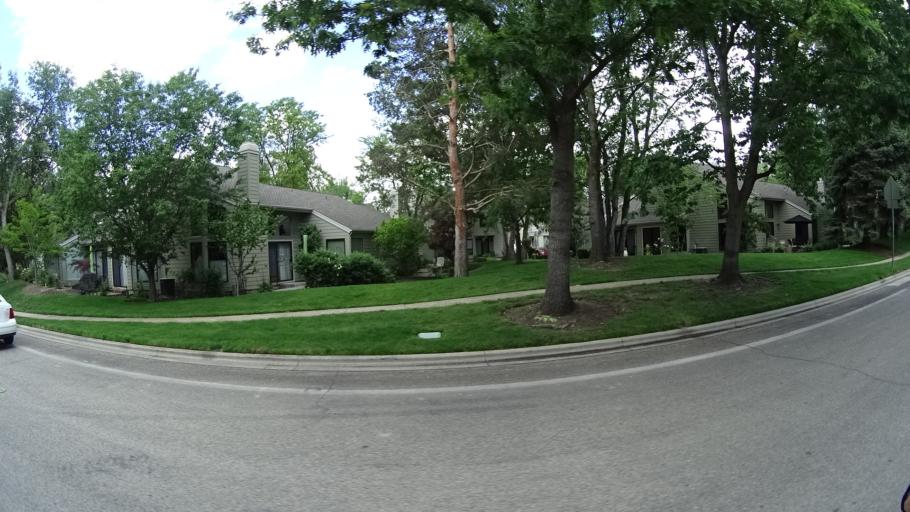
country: US
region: Idaho
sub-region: Ada County
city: Boise
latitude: 43.5882
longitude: -116.1701
